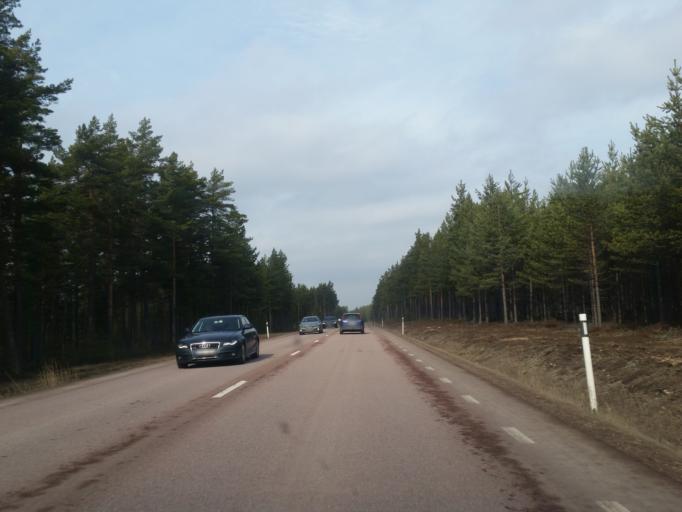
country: SE
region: Dalarna
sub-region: Leksand Municipality
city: Siljansnas
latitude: 60.9481
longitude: 14.7399
